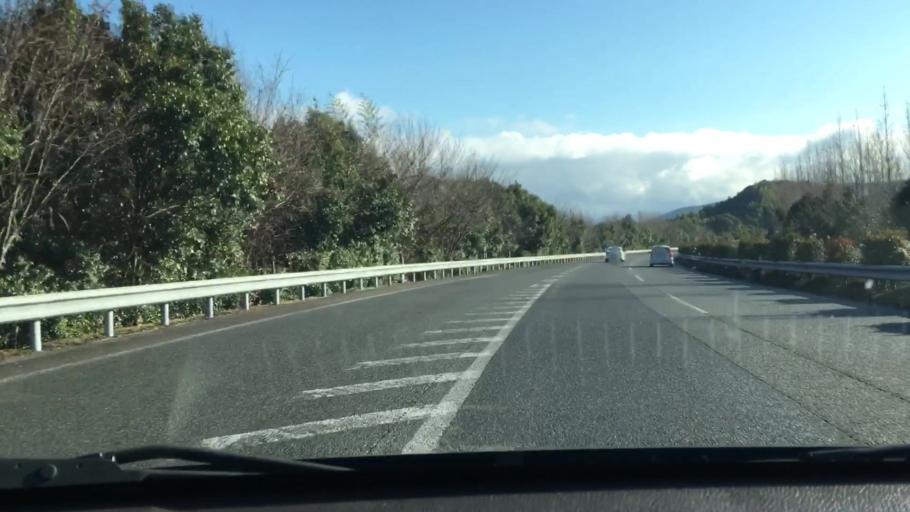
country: JP
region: Kumamoto
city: Hitoyoshi
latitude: 32.1980
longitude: 130.7771
